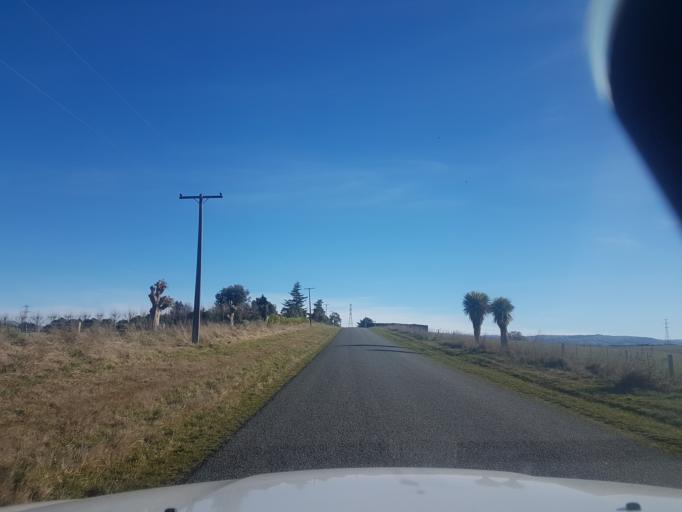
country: NZ
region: Canterbury
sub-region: Timaru District
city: Pleasant Point
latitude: -44.2531
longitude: 171.0456
